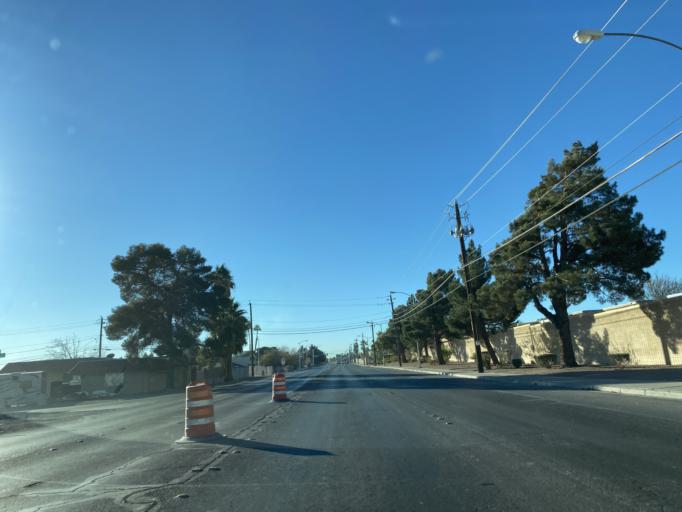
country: US
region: Nevada
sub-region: Clark County
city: Winchester
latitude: 36.1219
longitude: -115.0920
